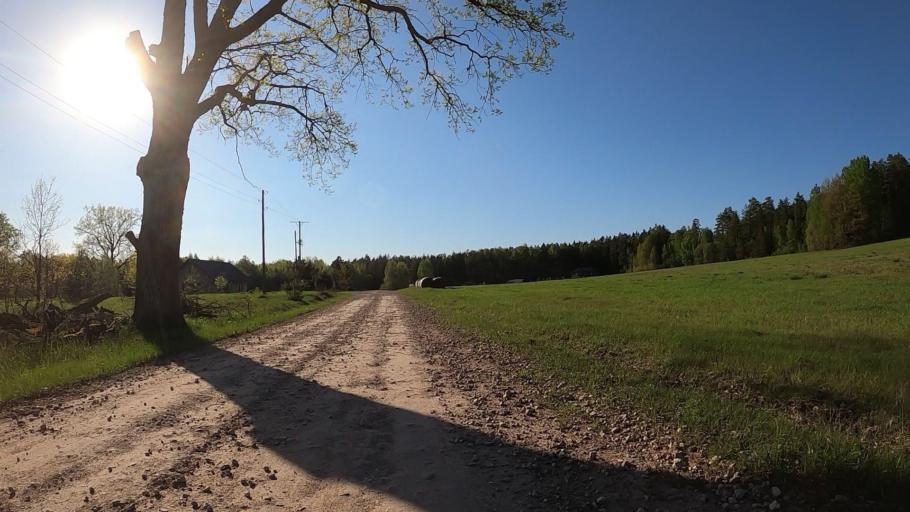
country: LV
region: Baldone
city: Baldone
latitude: 56.7633
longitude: 24.3744
